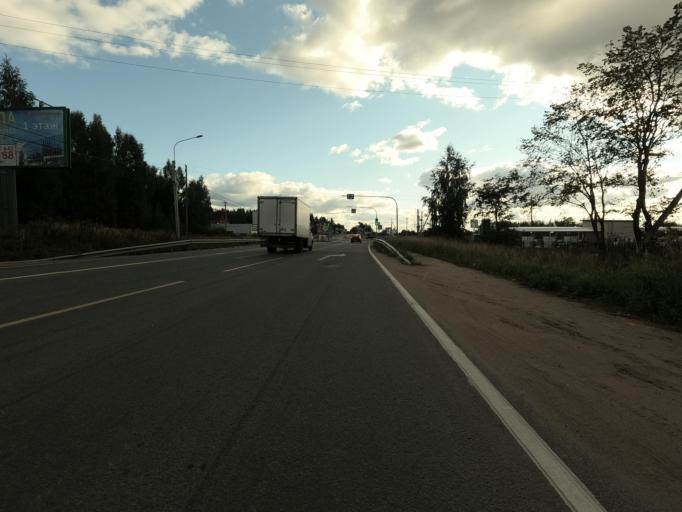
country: RU
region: Leningrad
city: Vsevolozhsk
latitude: 59.9874
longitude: 30.6564
